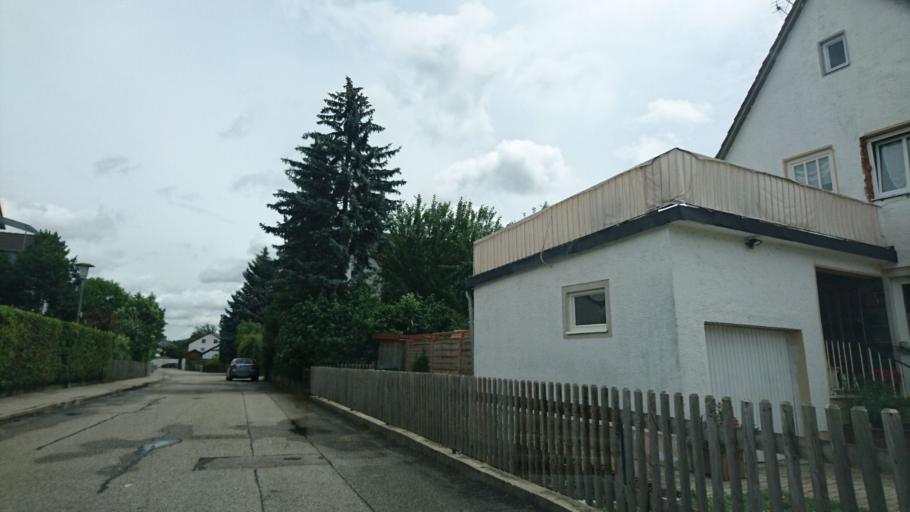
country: DE
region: Bavaria
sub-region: Lower Bavaria
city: Ergolding
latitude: 48.5561
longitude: 12.1654
